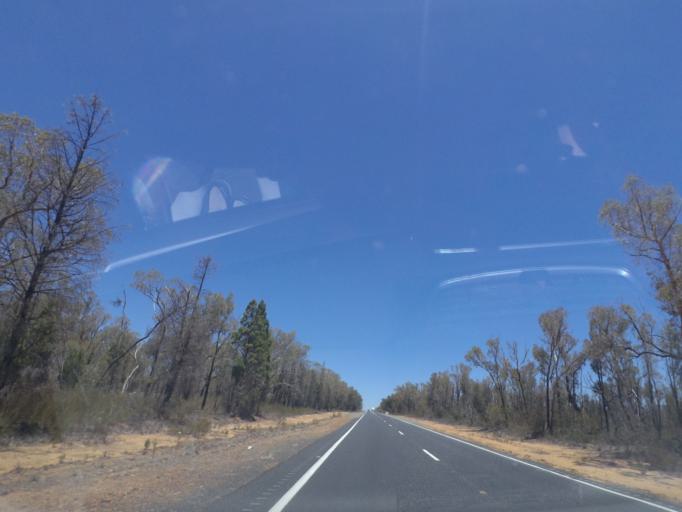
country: AU
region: New South Wales
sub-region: Warrumbungle Shire
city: Coonabarabran
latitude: -30.9592
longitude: 149.4200
